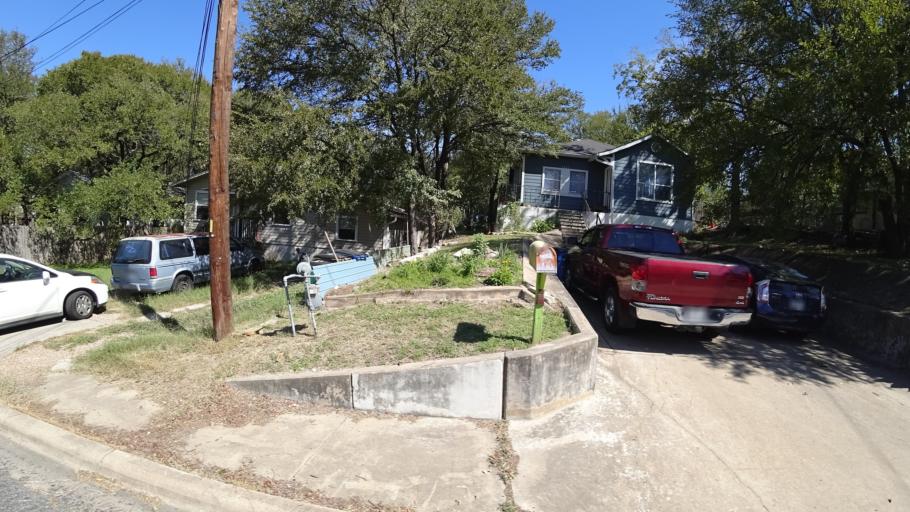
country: US
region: Texas
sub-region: Travis County
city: Austin
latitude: 30.2756
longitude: -97.6788
